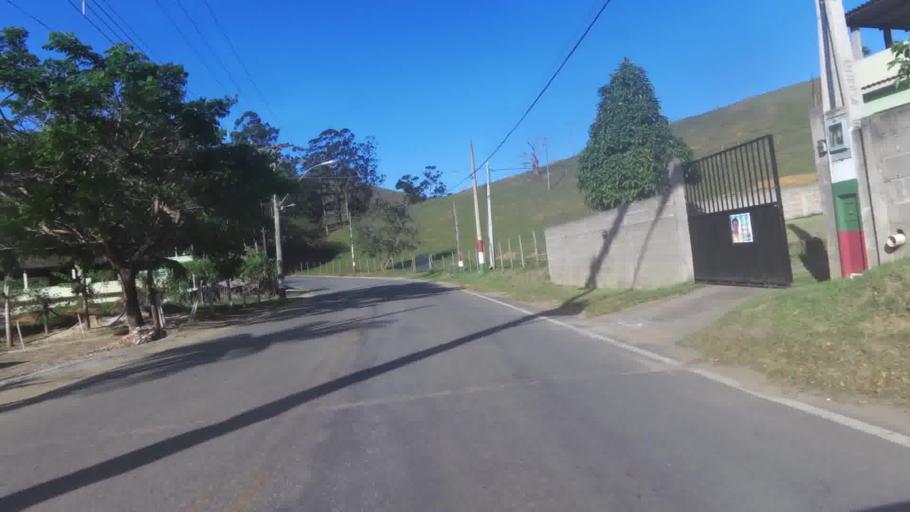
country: BR
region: Espirito Santo
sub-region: Iconha
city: Iconha
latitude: -20.7316
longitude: -40.7747
